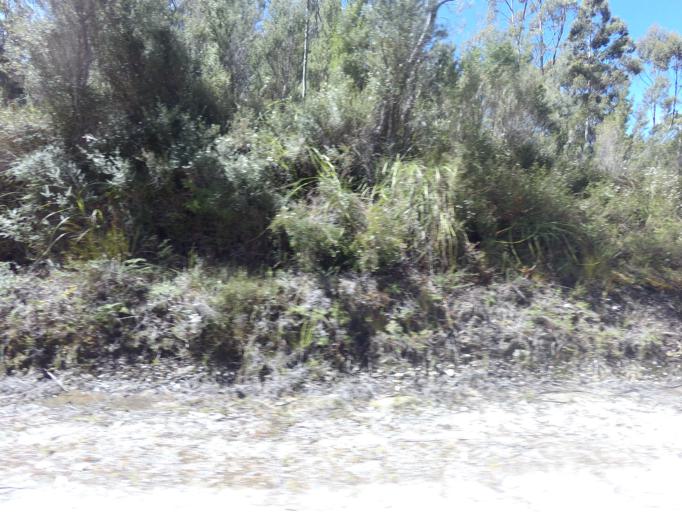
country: AU
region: Tasmania
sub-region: West Coast
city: Queenstown
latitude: -42.7663
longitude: 145.9867
